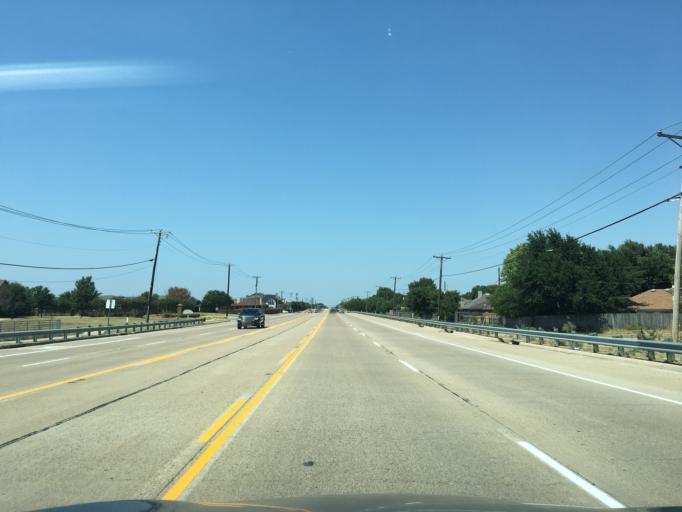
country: US
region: Texas
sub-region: Tarrant County
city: Edgecliff Village
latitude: 32.6267
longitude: -97.3485
